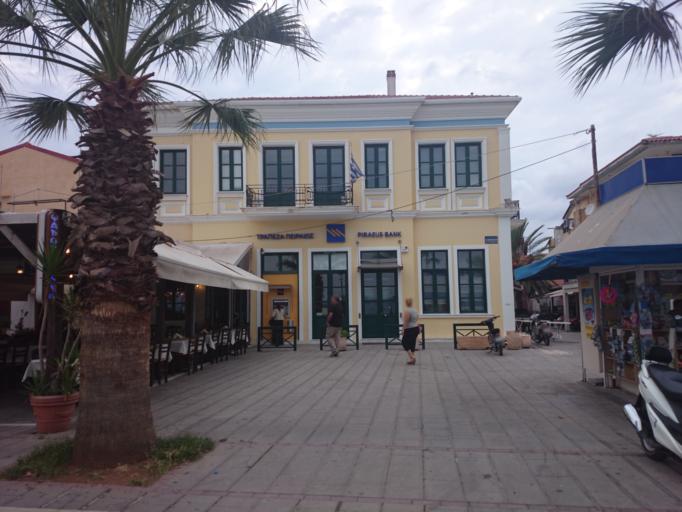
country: GR
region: Epirus
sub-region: Nomos Prevezis
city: Preveza
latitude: 38.9568
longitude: 20.7548
